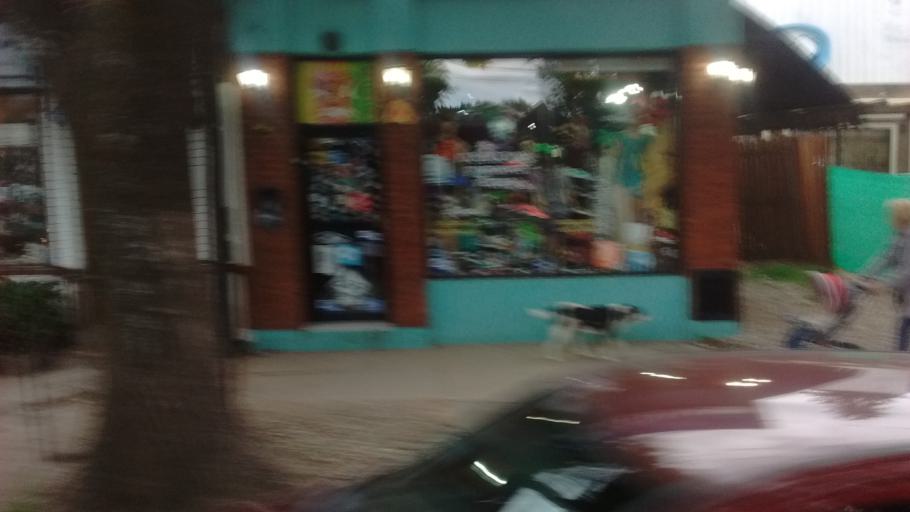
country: AR
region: Santa Fe
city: Funes
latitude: -32.9201
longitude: -60.8106
